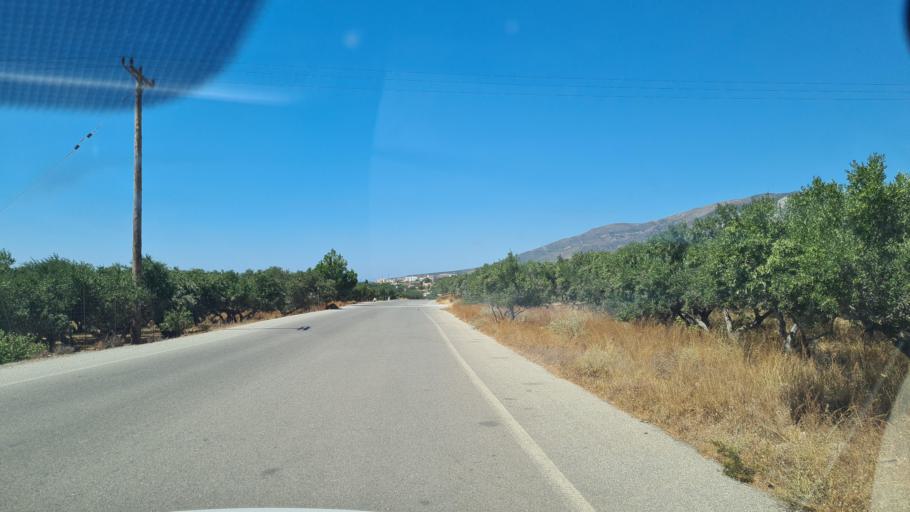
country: GR
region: Crete
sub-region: Nomos Chanias
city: Vryses
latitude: 35.3032
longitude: 23.5376
